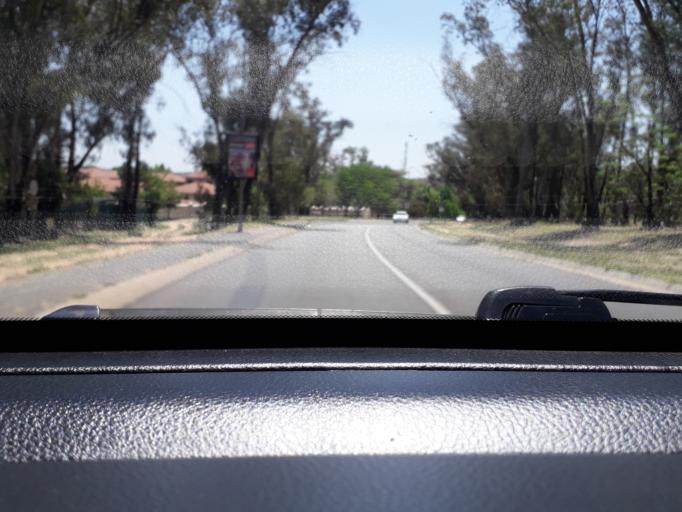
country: ZA
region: Gauteng
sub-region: City of Johannesburg Metropolitan Municipality
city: Midrand
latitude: -26.0459
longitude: 28.0699
